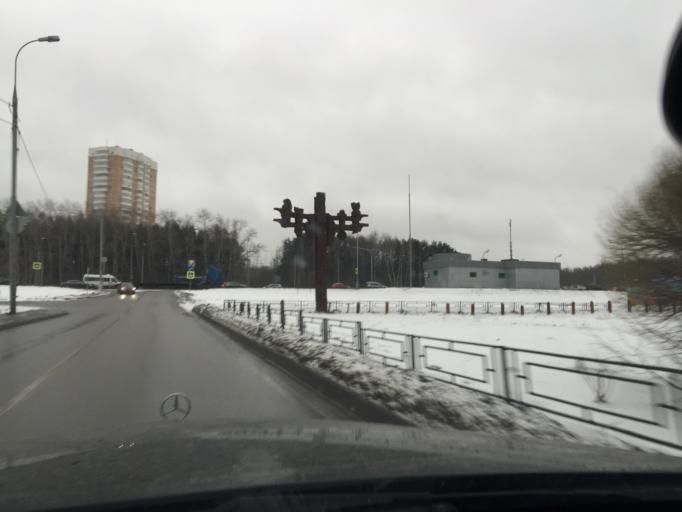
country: RU
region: Moscow
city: Troparevo
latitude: 55.6438
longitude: 37.4672
